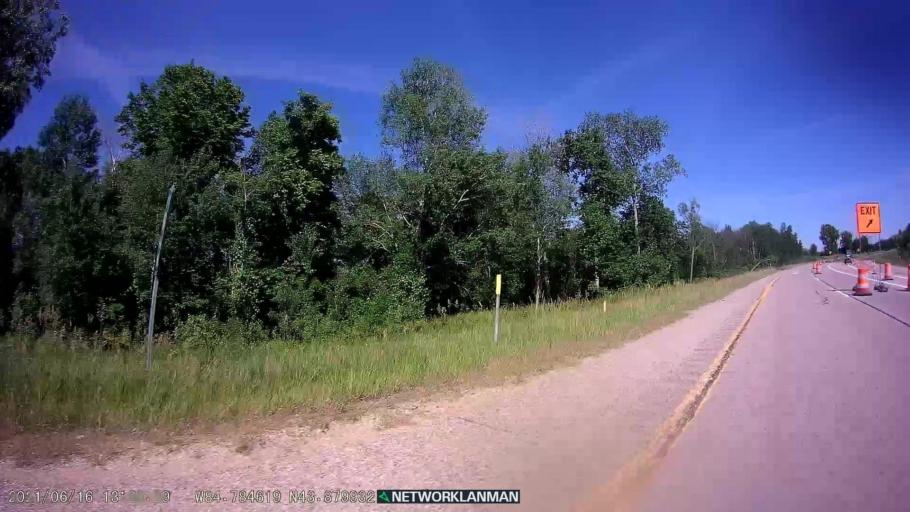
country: US
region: Michigan
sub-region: Clare County
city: Clare
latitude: 43.8793
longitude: -84.7861
